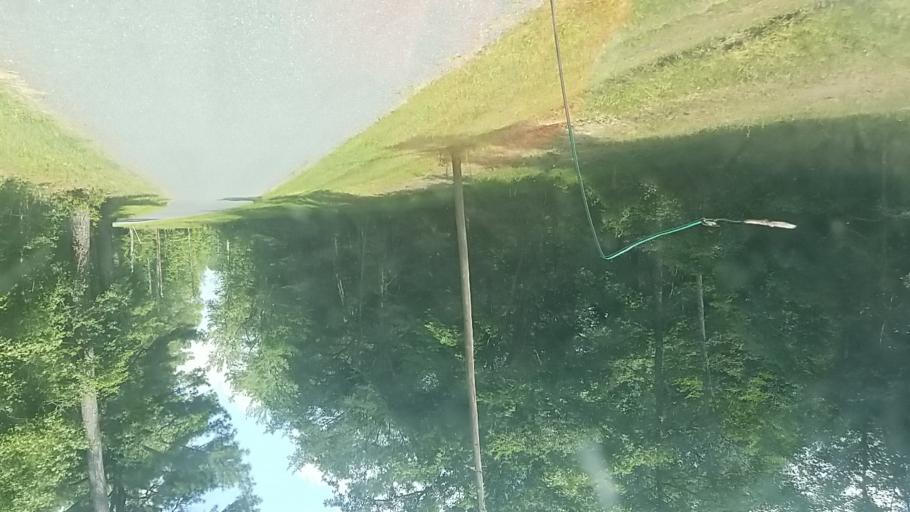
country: US
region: Maryland
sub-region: Worcester County
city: Snow Hill
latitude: 38.2494
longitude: -75.4221
